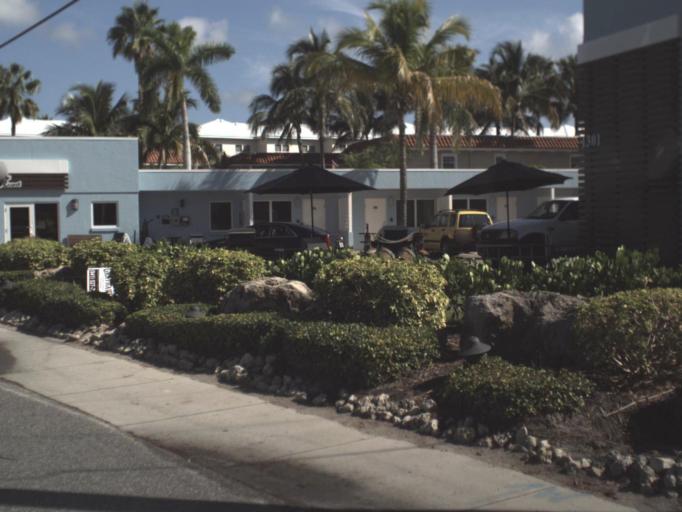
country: US
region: Florida
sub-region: Manatee County
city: Bradenton Beach
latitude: 27.4726
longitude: -82.7011
